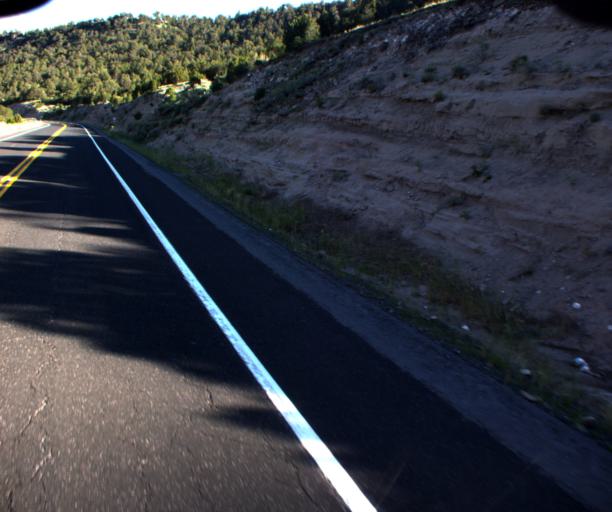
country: US
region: Arizona
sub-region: Apache County
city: Eagar
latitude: 34.0560
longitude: -109.1890
